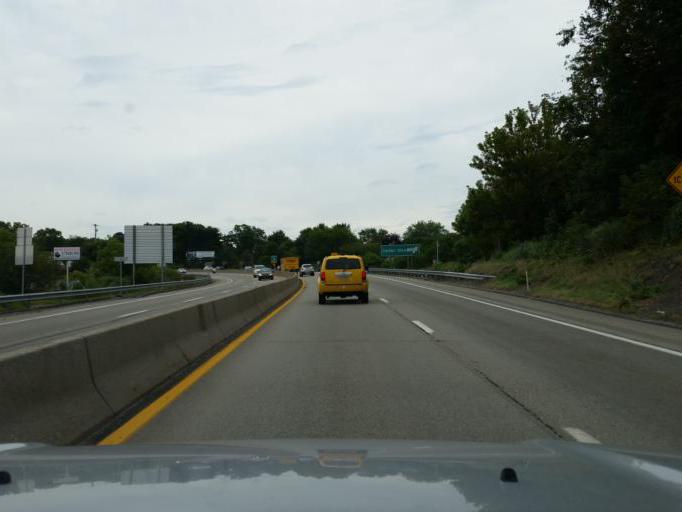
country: US
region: Pennsylvania
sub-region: Westmoreland County
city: South Greensburg
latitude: 40.2841
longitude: -79.5423
